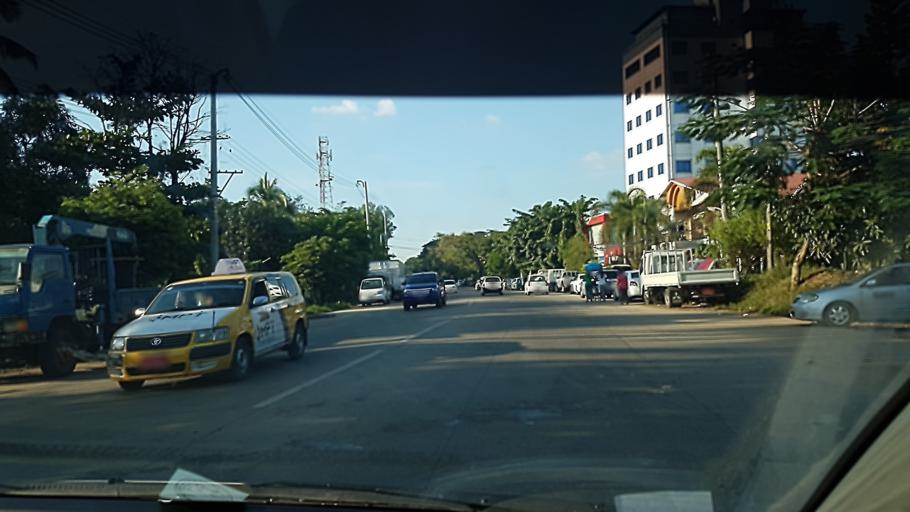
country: MM
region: Yangon
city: Yangon
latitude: 16.8313
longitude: 96.1884
